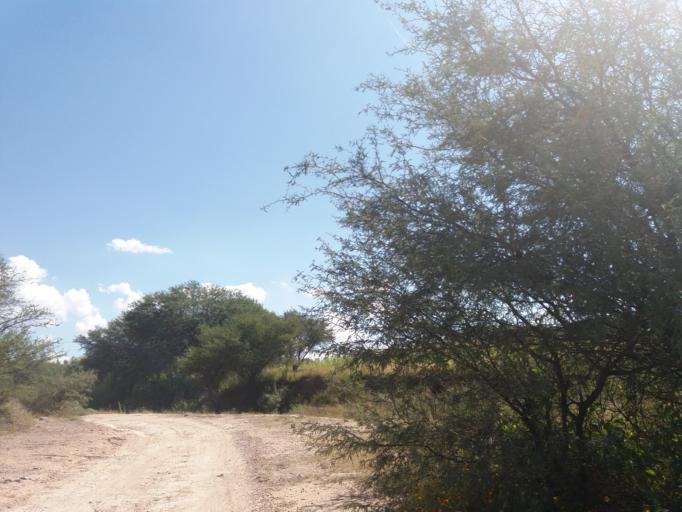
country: MX
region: Aguascalientes
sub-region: Aguascalientes
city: Penuelas (El Cienegal)
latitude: 21.7663
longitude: -102.2358
